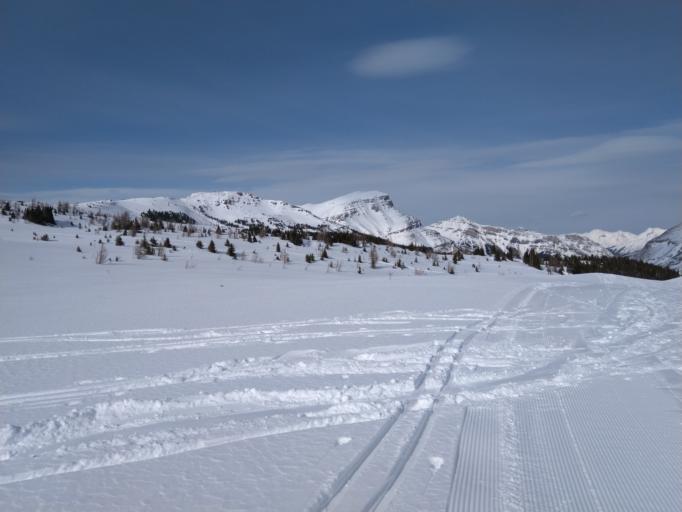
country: CA
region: Alberta
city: Banff
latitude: 51.0819
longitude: -115.7917
